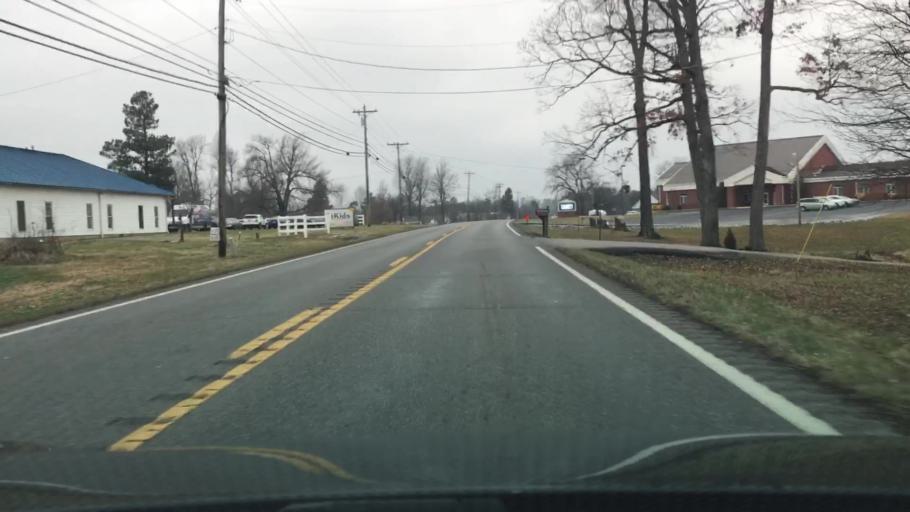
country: US
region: Kentucky
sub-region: Marshall County
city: Benton
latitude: 36.9415
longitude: -88.3614
